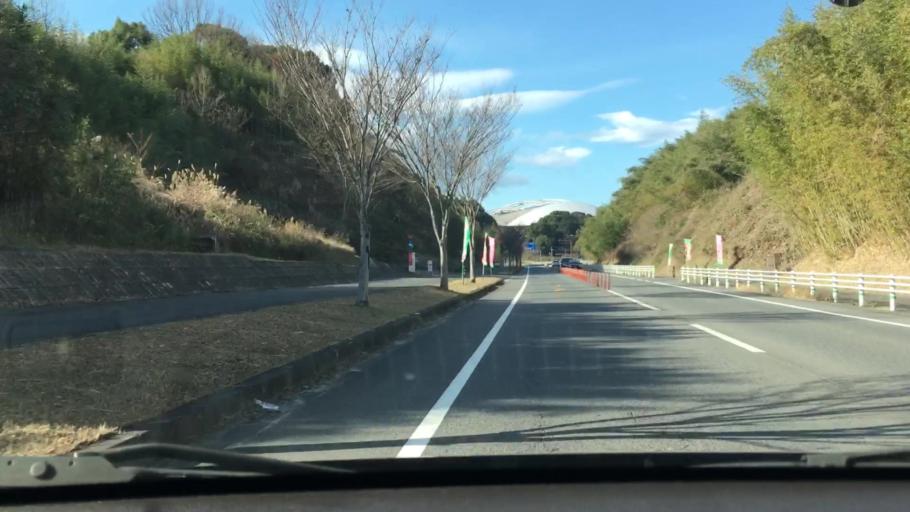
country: JP
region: Oita
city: Tsurusaki
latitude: 33.1923
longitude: 131.6678
